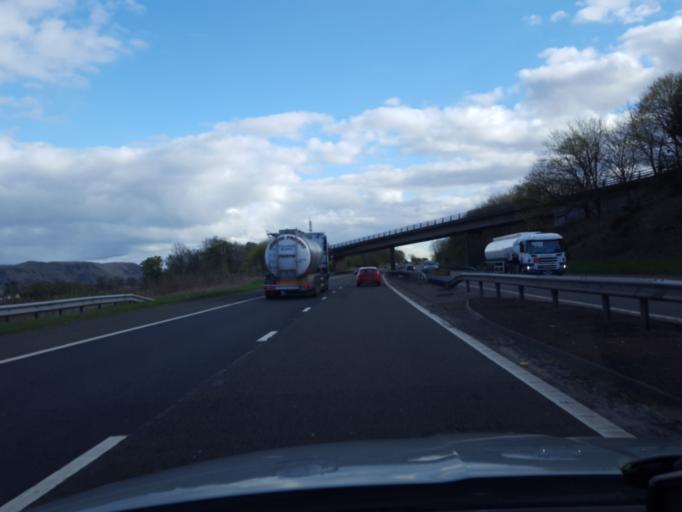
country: GB
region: Scotland
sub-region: Perth and Kinross
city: Milnathort
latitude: 56.2635
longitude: -3.3798
